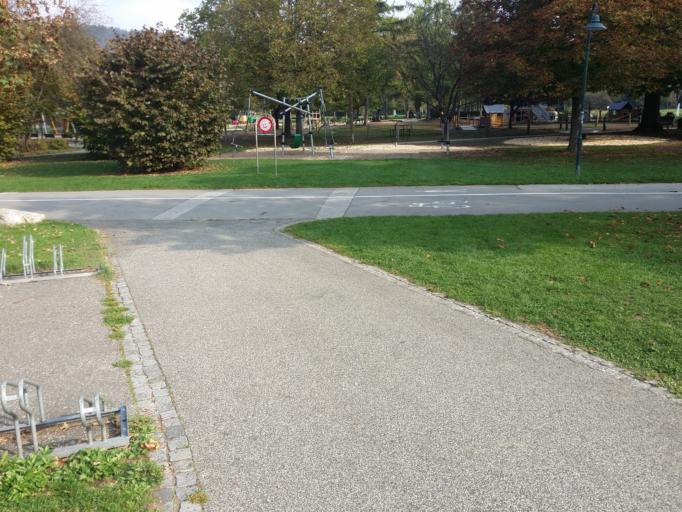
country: AT
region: Carinthia
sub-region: Klagenfurt am Woerthersee
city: Klagenfurt am Woerthersee
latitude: 46.6190
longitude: 14.2592
